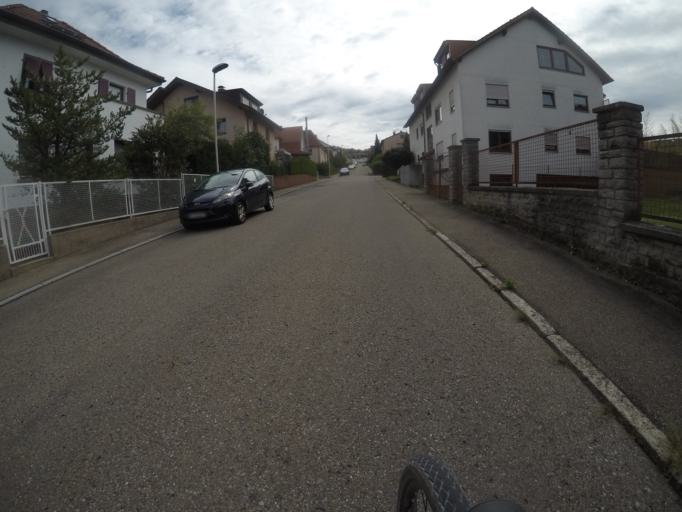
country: DE
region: Baden-Wuerttemberg
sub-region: Karlsruhe Region
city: Niefern-Oschelbronn
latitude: 48.9202
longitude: 8.7876
